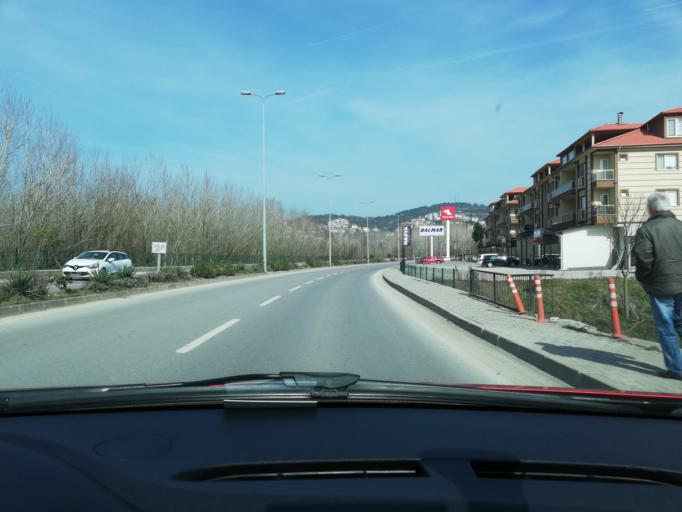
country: TR
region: Bartin
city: Bartin
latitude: 41.6330
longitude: 32.3487
